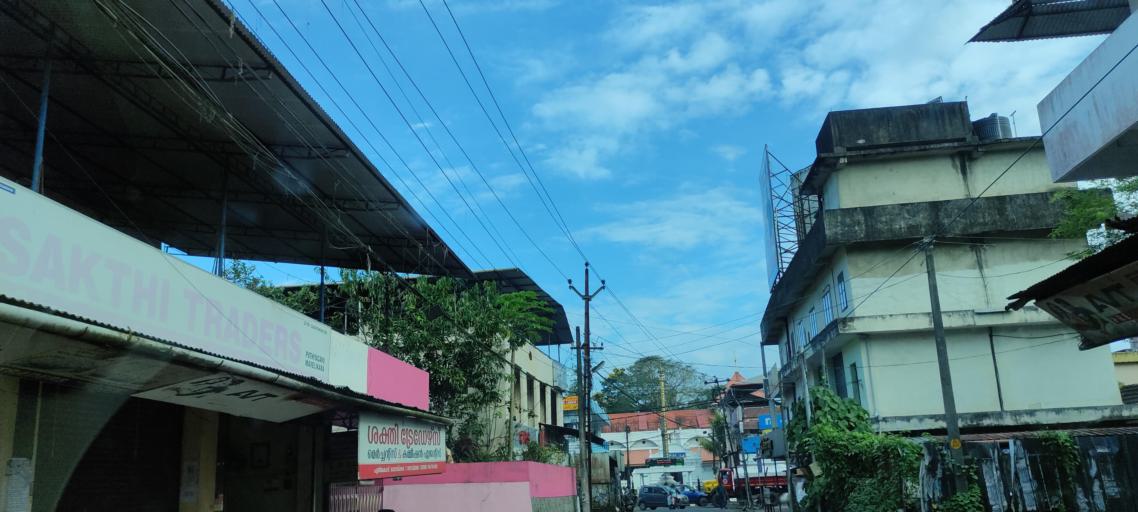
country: IN
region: Kerala
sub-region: Alappuzha
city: Mavelikara
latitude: 9.2530
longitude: 76.5470
